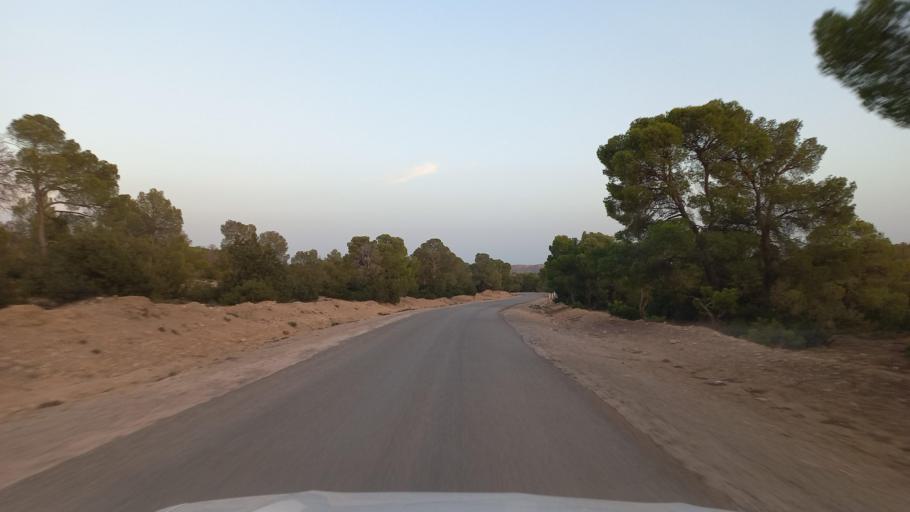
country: TN
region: Al Qasrayn
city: Sbiba
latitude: 35.4121
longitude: 8.9437
